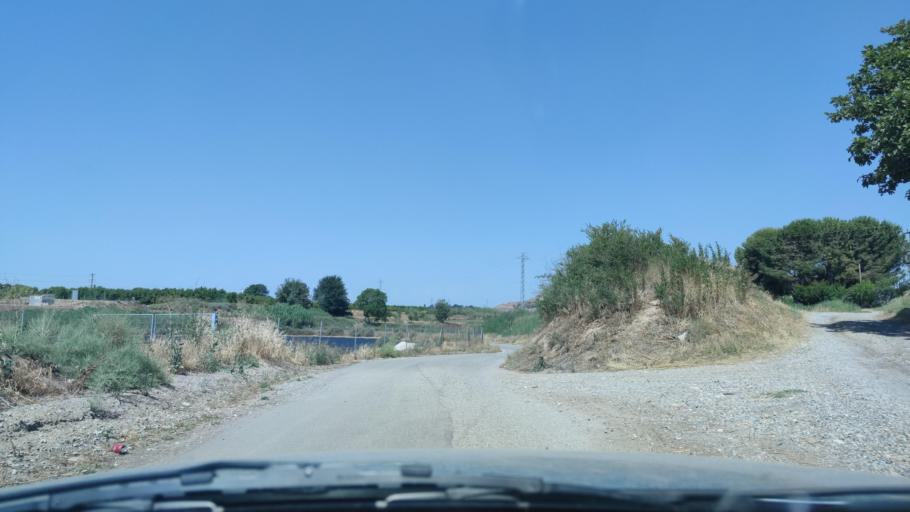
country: ES
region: Catalonia
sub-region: Provincia de Lleida
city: Torrefarrera
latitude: 41.6695
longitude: 0.5924
